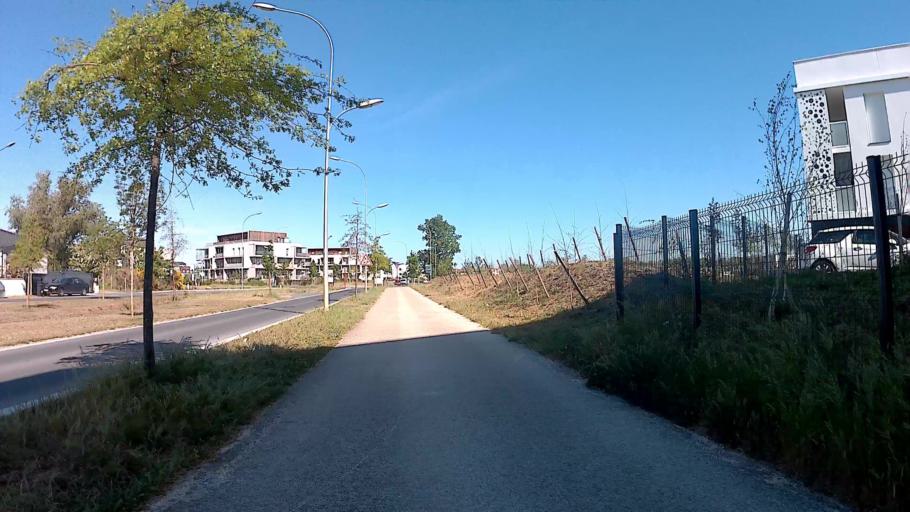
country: FR
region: Aquitaine
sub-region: Departement de la Gironde
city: Villenave-d'Ornon
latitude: 44.7758
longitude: -0.5289
